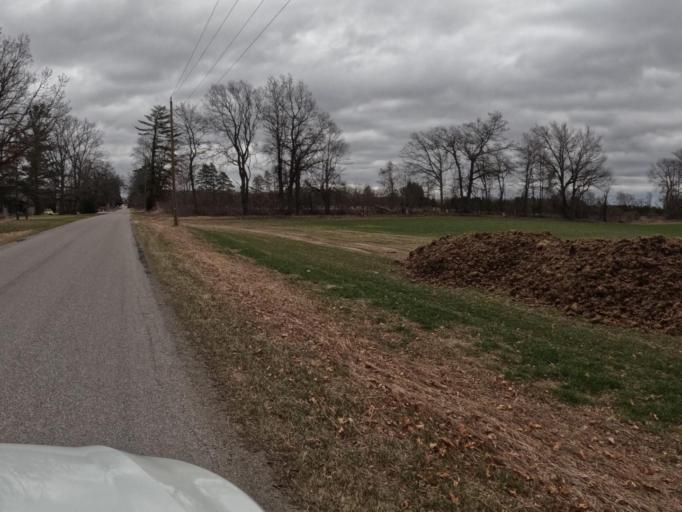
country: CA
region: Ontario
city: Norfolk County
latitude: 42.9383
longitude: -80.4350
